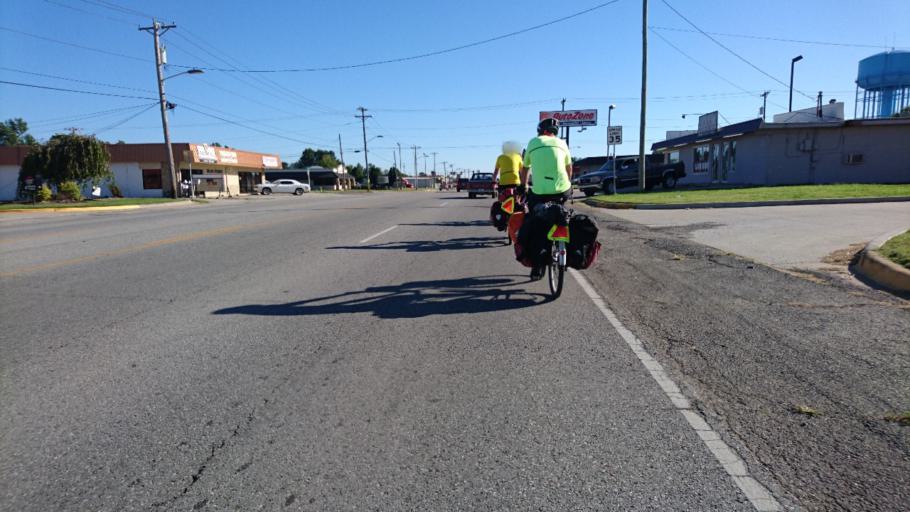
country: US
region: Oklahoma
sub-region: Ottawa County
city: Miami
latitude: 36.8907
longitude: -94.8776
